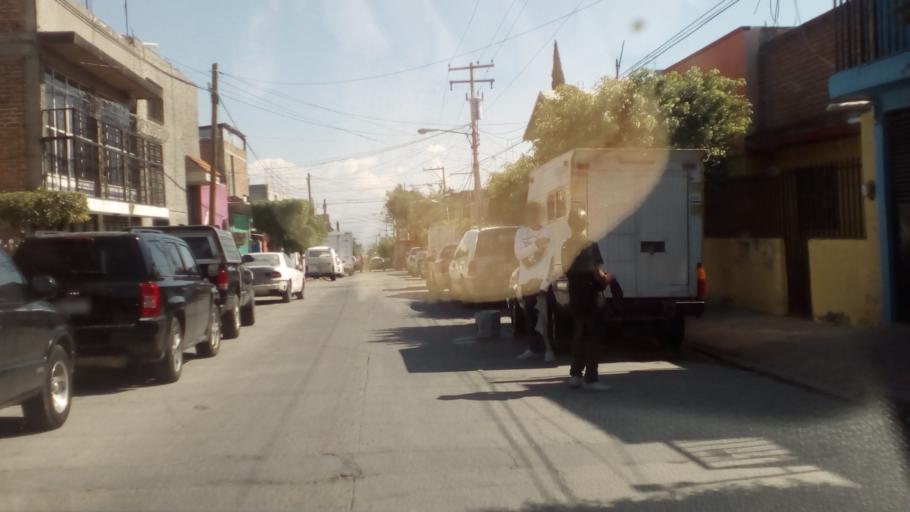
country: MX
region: Guanajuato
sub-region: Leon
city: Ejido la Joya
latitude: 21.1274
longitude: -101.7127
